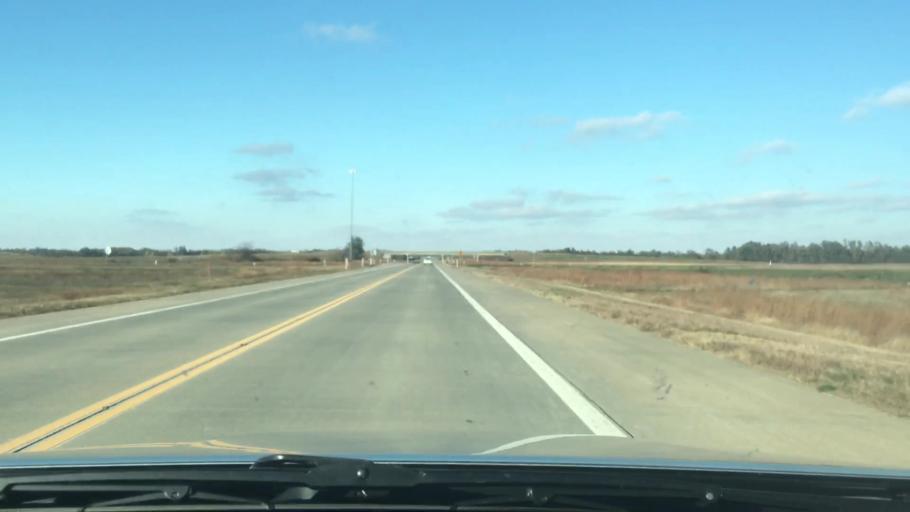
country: US
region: Kansas
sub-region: Reno County
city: South Hutchinson
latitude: 38.0363
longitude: -97.9857
